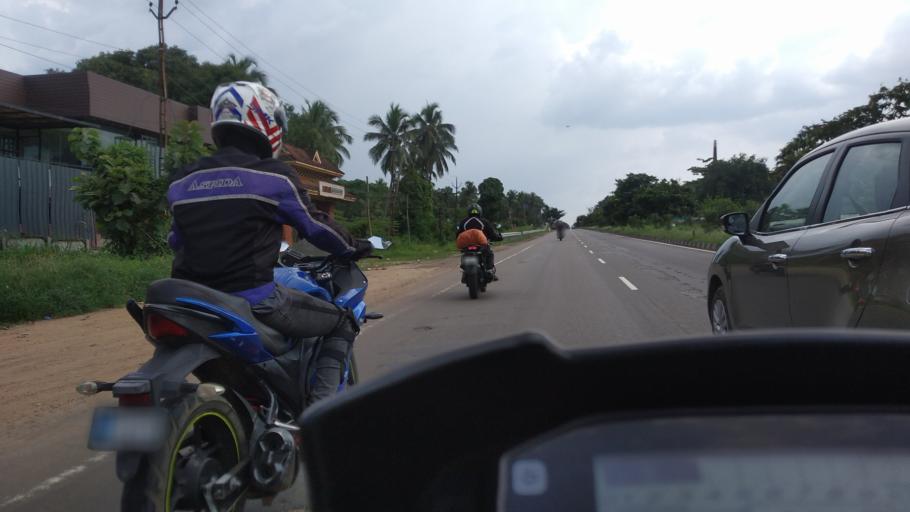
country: IN
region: Kerala
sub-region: Thrissur District
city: Trichur
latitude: 10.4824
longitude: 76.2579
